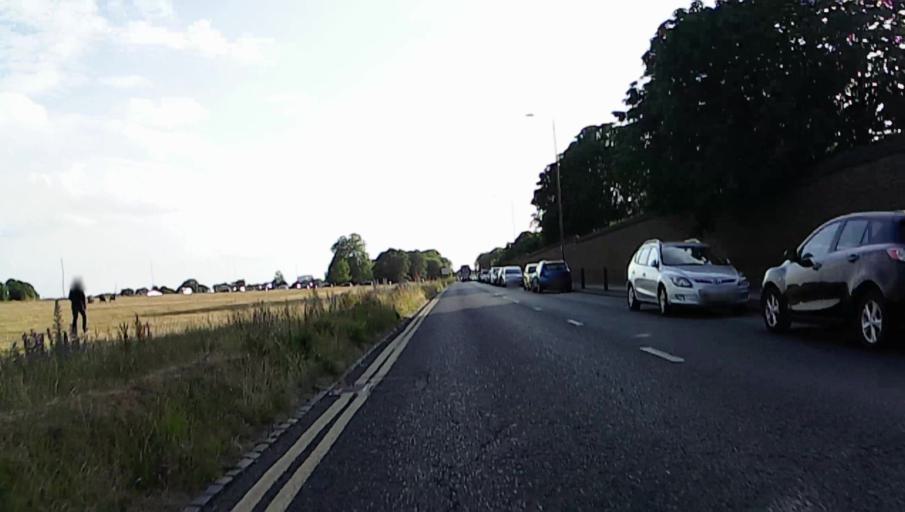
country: GB
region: England
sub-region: Greater London
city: Blackheath
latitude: 51.4735
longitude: 0.0070
